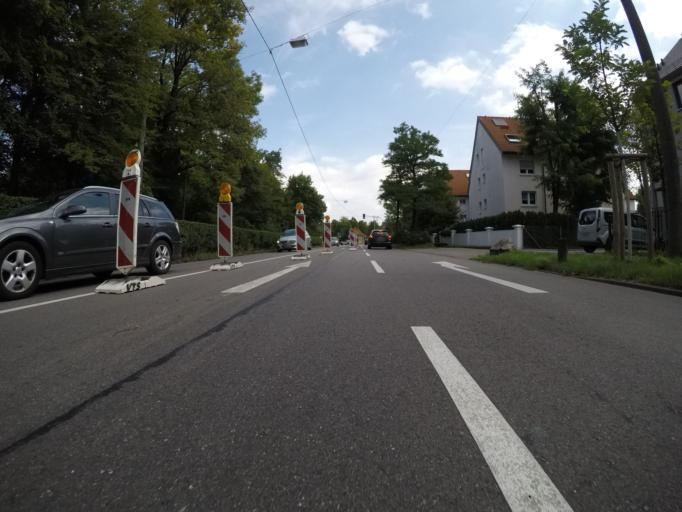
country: DE
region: Baden-Wuerttemberg
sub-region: Regierungsbezirk Stuttgart
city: Stuttgart Feuerbach
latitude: 48.7867
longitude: 9.1503
